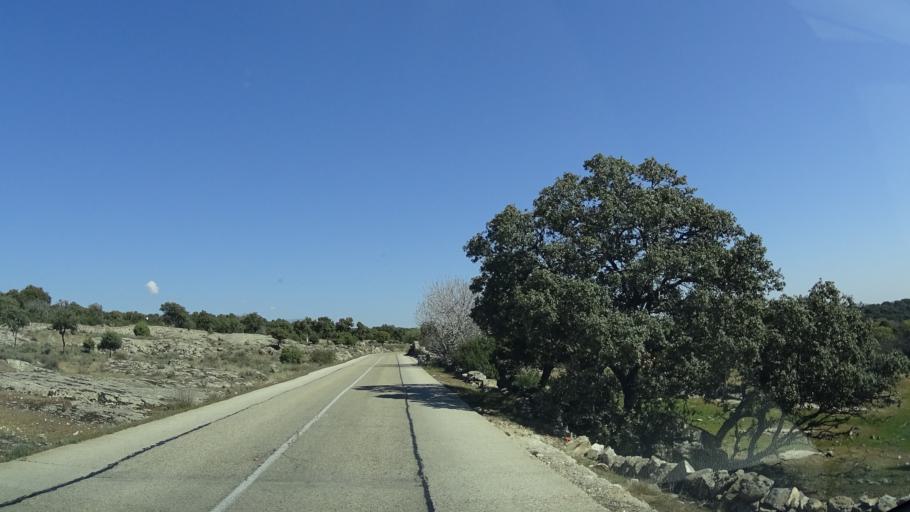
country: ES
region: Madrid
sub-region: Provincia de Madrid
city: Hoyo de Manzanares
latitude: 40.6402
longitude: -3.8478
